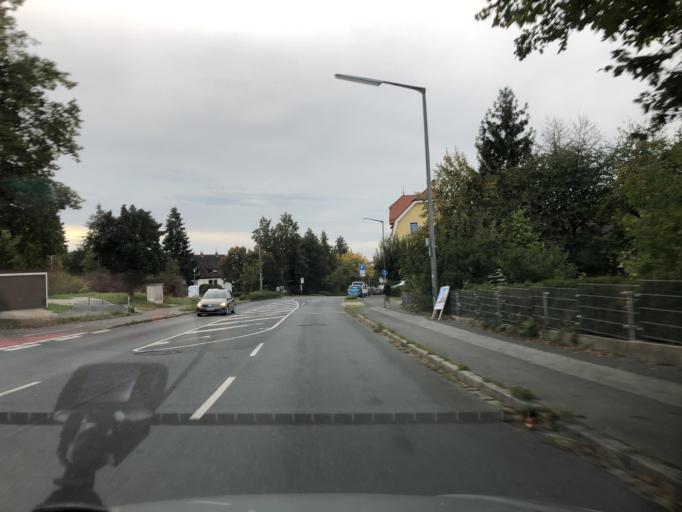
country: DE
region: Bavaria
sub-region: Regierungsbezirk Mittelfranken
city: Zirndorf
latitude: 49.4365
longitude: 10.9697
